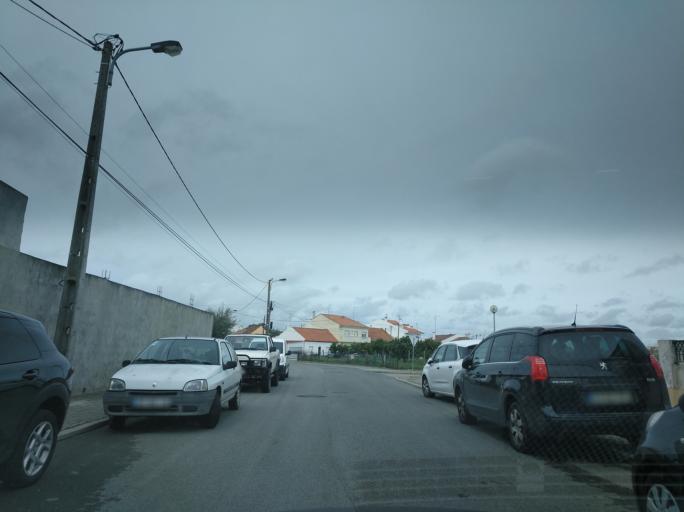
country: PT
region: Setubal
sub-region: Grandola
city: Grandola
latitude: 38.1813
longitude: -8.5718
